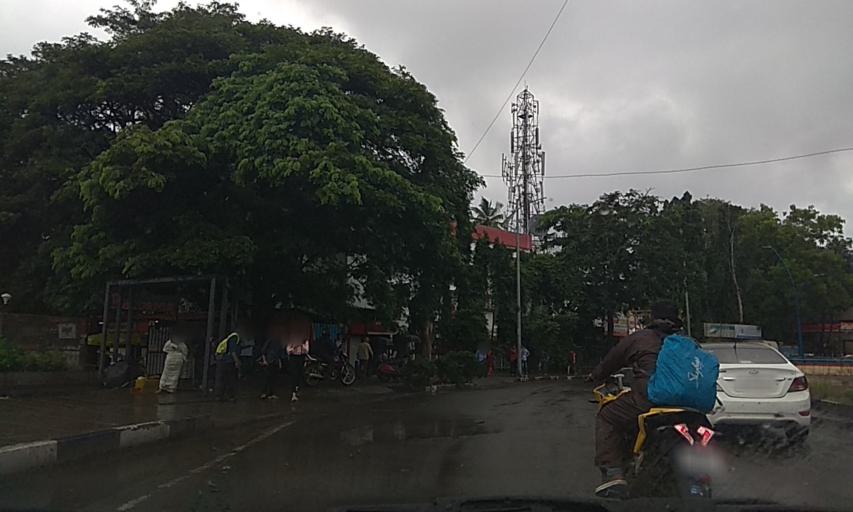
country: IN
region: Maharashtra
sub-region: Pune Division
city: Shivaji Nagar
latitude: 18.5275
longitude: 73.8511
